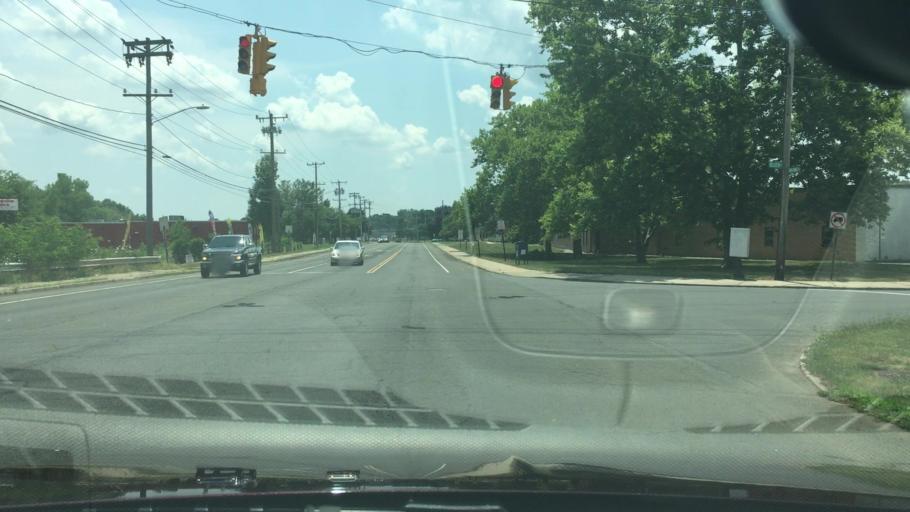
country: US
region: Connecticut
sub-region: Hartford County
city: New Britain
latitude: 41.6677
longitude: -72.7549
